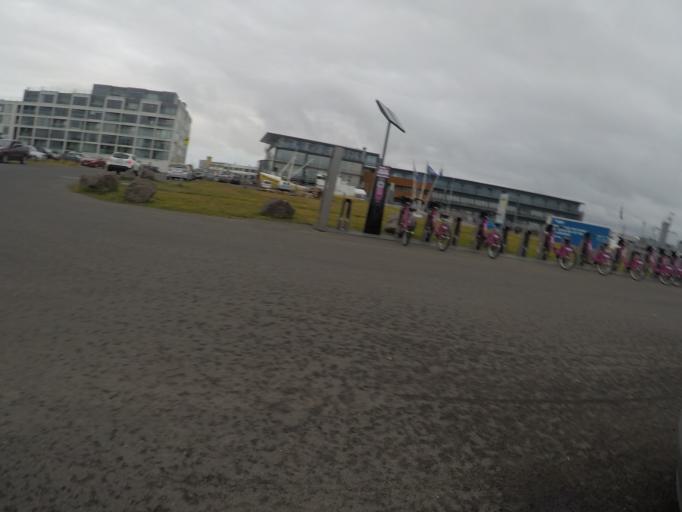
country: IS
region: Capital Region
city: Seltjarnarnes
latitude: 64.1521
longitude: -21.9473
